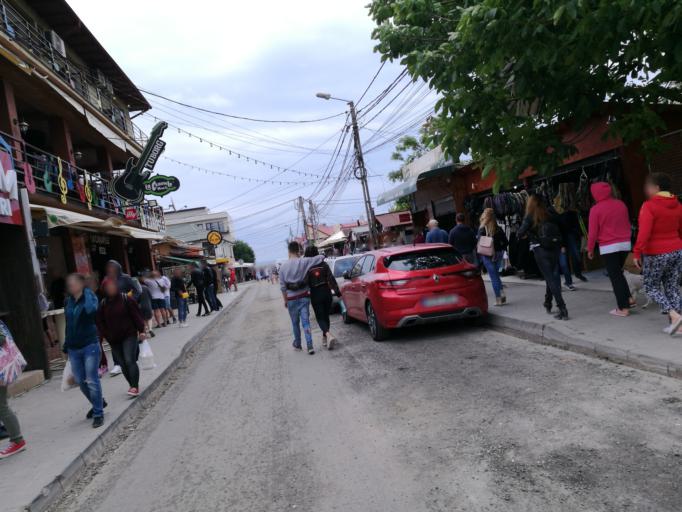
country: RO
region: Constanta
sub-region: Municipiul Mangalia
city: Mangalia
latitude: 43.7534
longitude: 28.5724
